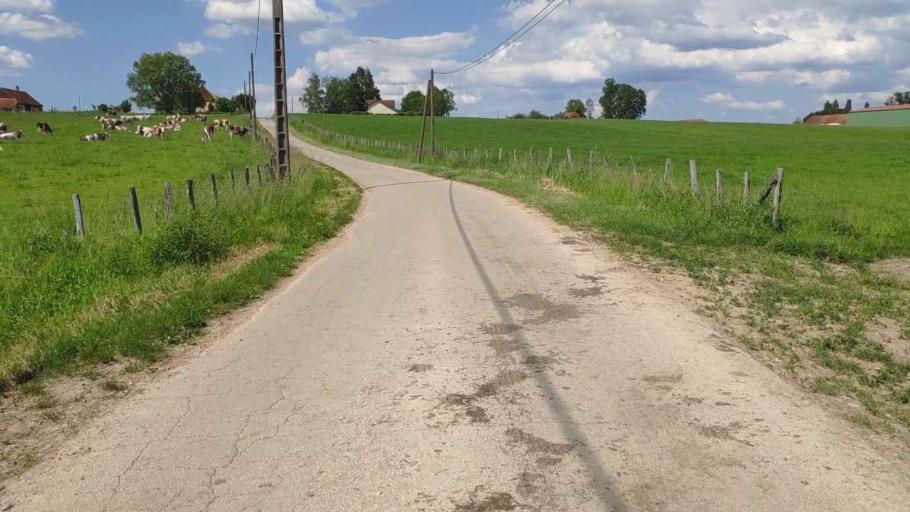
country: FR
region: Franche-Comte
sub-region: Departement du Jura
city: Bletterans
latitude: 46.8220
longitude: 5.4006
